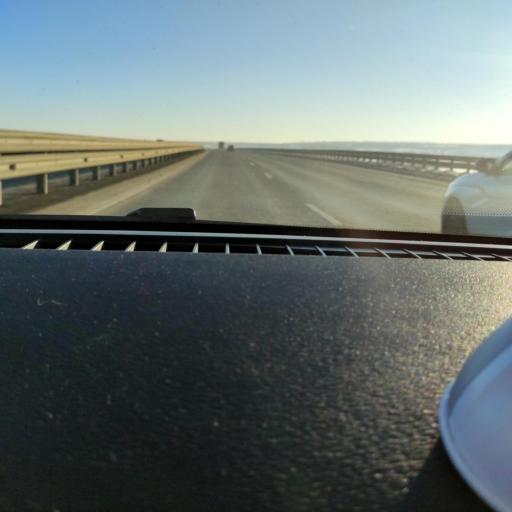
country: RU
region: Samara
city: Smyshlyayevka
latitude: 53.1584
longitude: 50.3328
